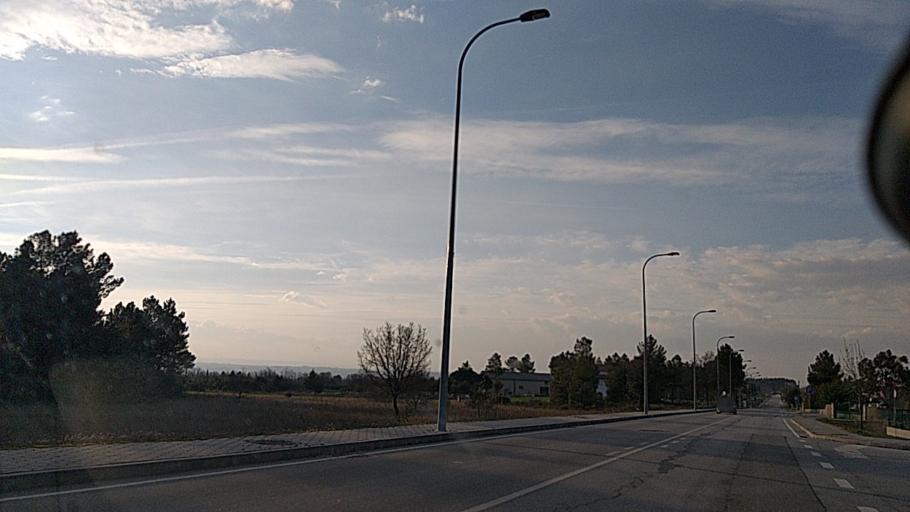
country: ES
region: Castille and Leon
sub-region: Provincia de Salamanca
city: Fuentes de Onoro
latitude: 40.5973
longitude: -6.9952
